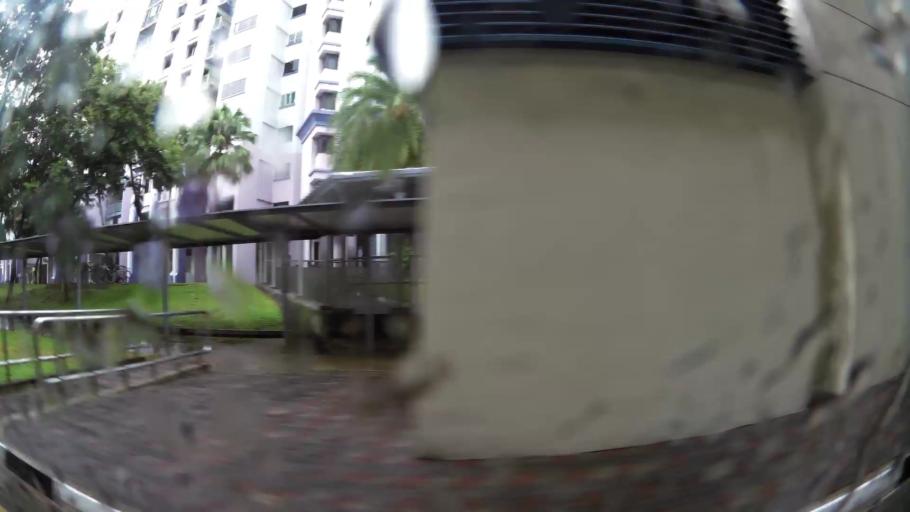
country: MY
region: Johor
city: Kampung Pasir Gudang Baru
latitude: 1.3840
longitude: 103.9021
